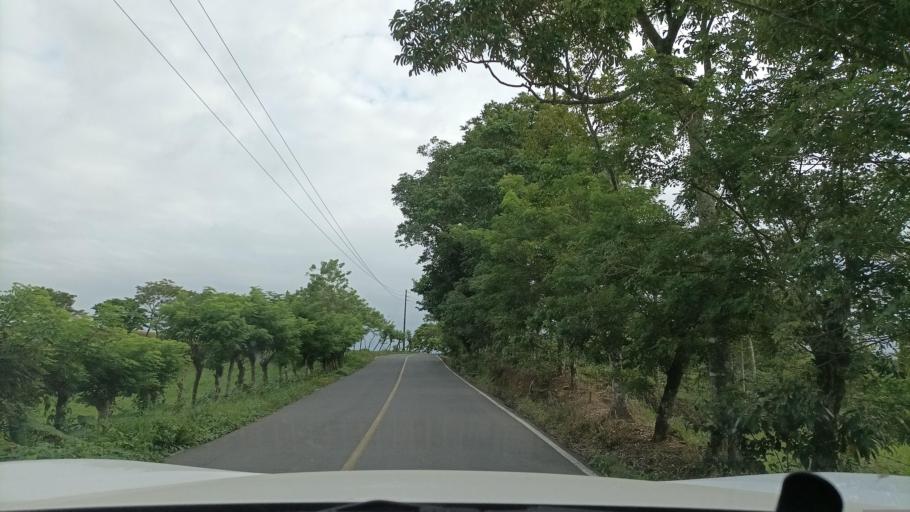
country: MX
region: Veracruz
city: Hidalgotitlan
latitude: 17.6881
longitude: -94.4635
